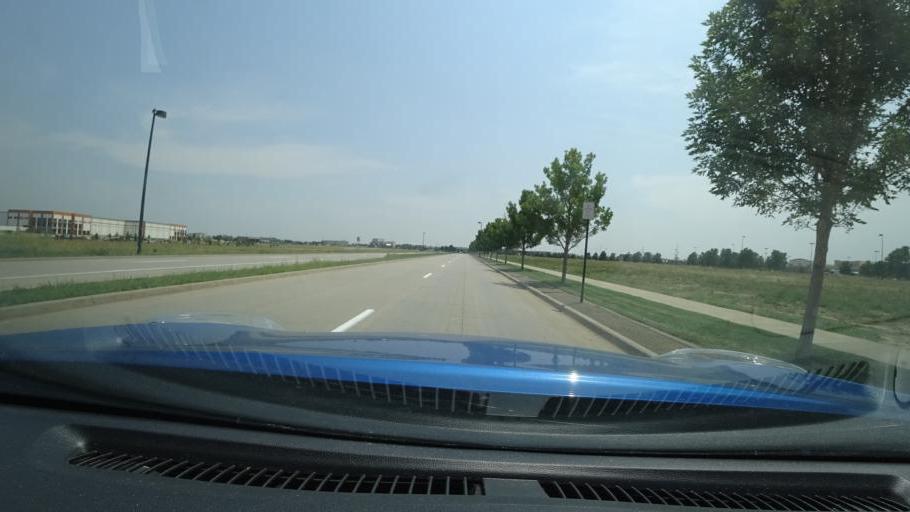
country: US
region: Colorado
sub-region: Adams County
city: Aurora
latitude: 39.7663
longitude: -104.7805
